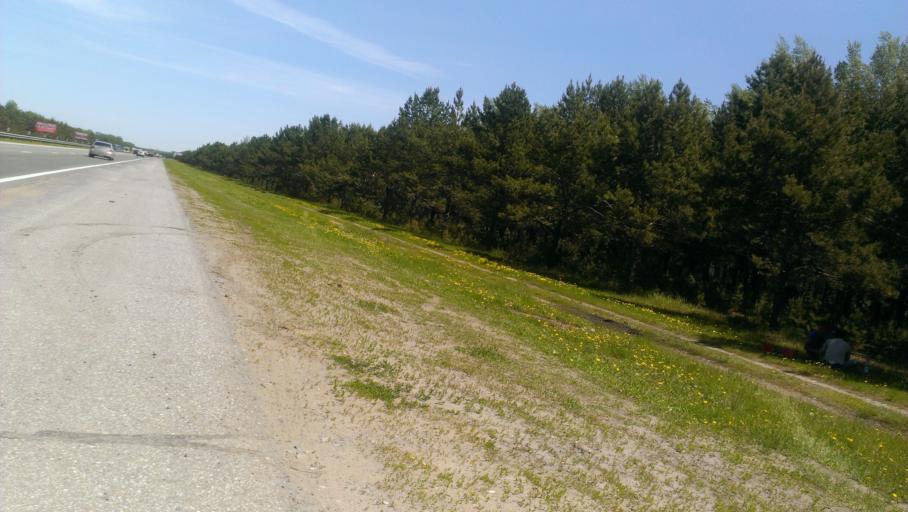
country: RU
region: Altai Krai
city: Zaton
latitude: 53.3186
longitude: 83.8781
